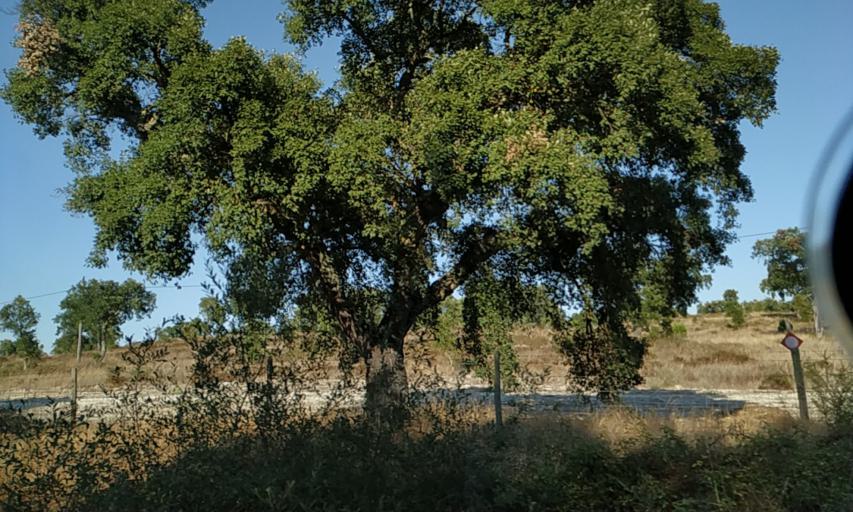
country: PT
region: Santarem
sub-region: Almeirim
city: Fazendas de Almeirim
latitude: 39.0720
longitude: -8.5655
